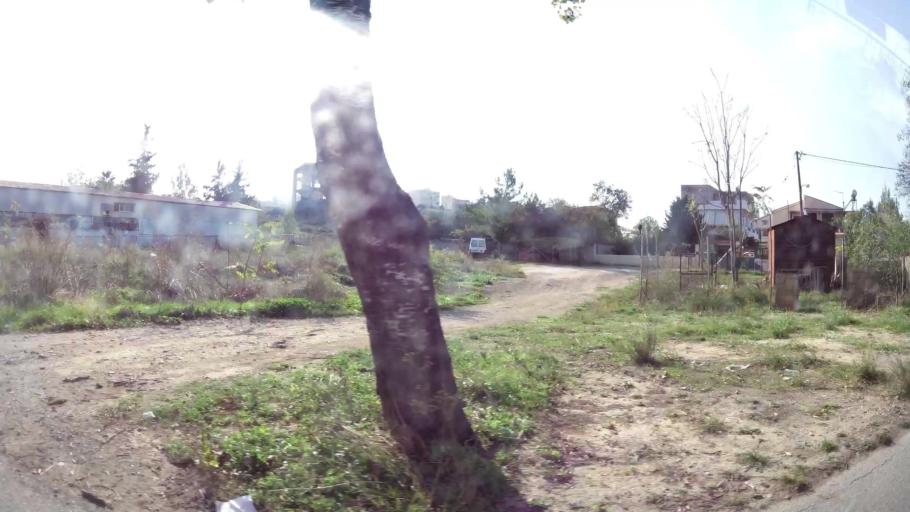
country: GR
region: Attica
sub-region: Nomarchia Anatolikis Attikis
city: Acharnes
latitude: 38.0711
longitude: 23.7317
